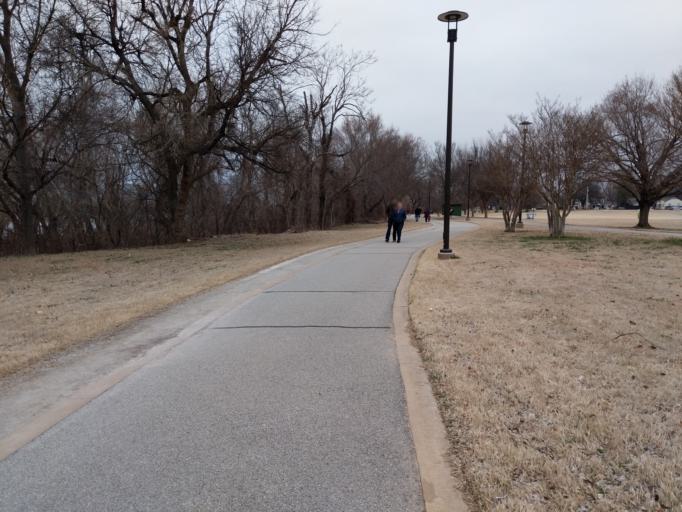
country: US
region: Oklahoma
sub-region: Tulsa County
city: Tulsa
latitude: 36.1078
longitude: -95.9841
